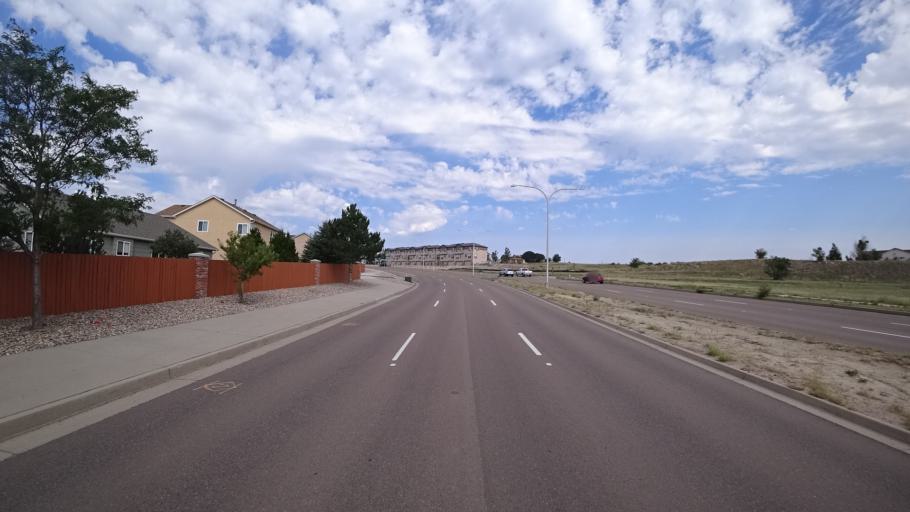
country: US
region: Colorado
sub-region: El Paso County
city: Cimarron Hills
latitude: 38.9115
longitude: -104.7236
